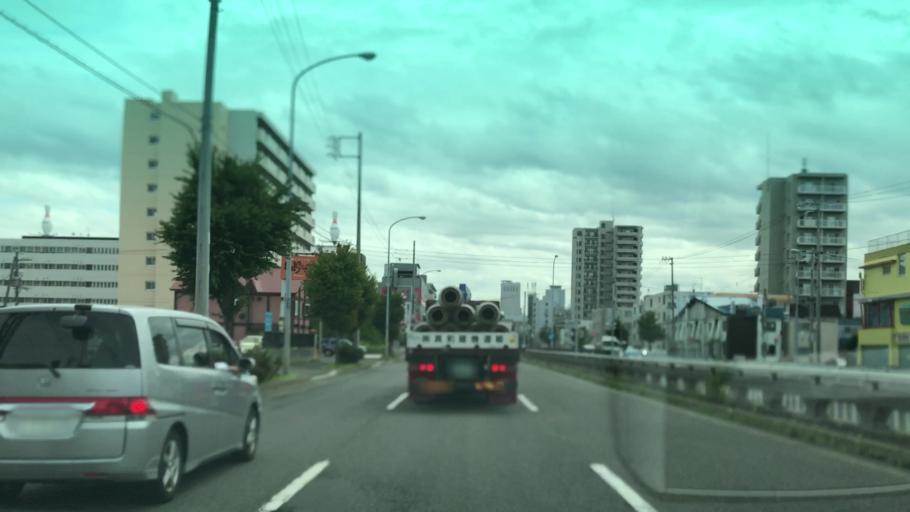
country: JP
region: Hokkaido
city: Sapporo
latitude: 43.0886
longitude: 141.3484
